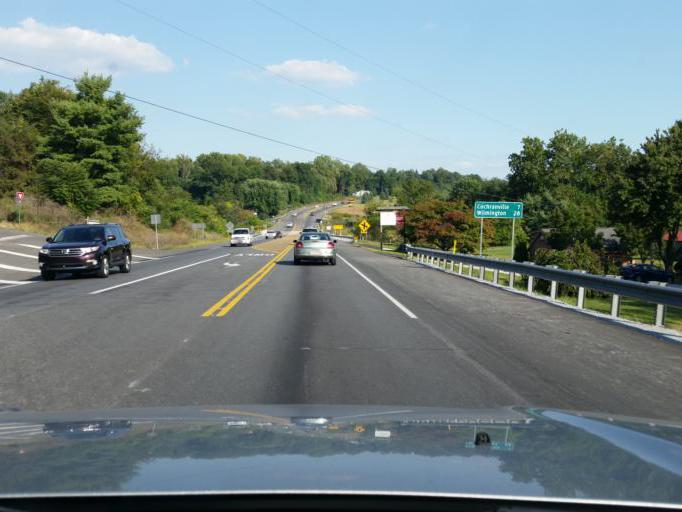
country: US
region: Pennsylvania
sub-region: Lancaster County
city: Christiana
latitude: 39.9624
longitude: -75.9908
